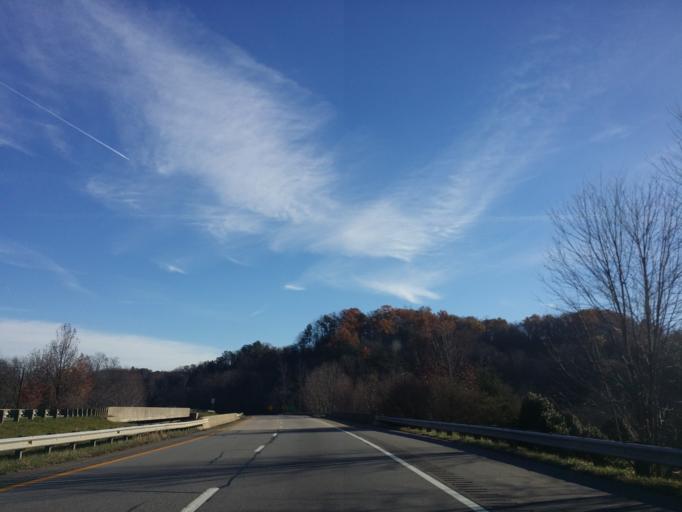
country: US
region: North Carolina
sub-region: Buncombe County
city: Black Mountain
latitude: 35.6224
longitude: -82.1817
